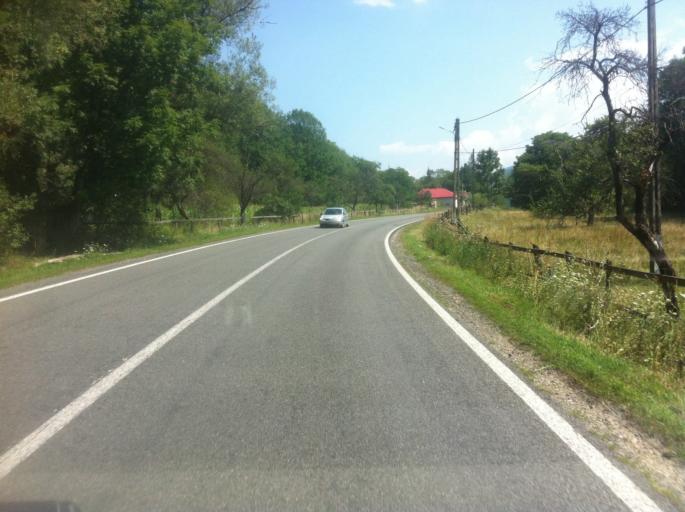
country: RO
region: Caras-Severin
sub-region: Comuna Bautar
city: Bucova
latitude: 45.5127
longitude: 22.6338
